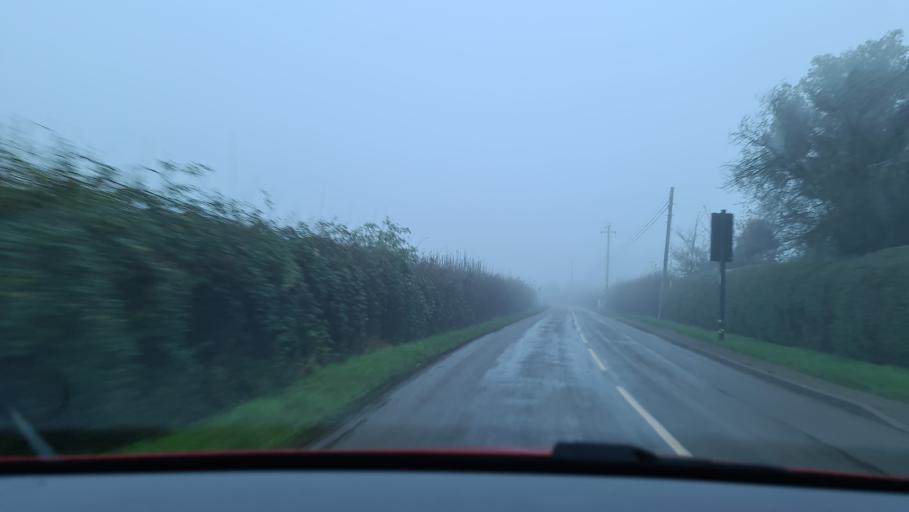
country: GB
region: England
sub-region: Buckinghamshire
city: Waddesdon
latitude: 51.8758
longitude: -0.9241
